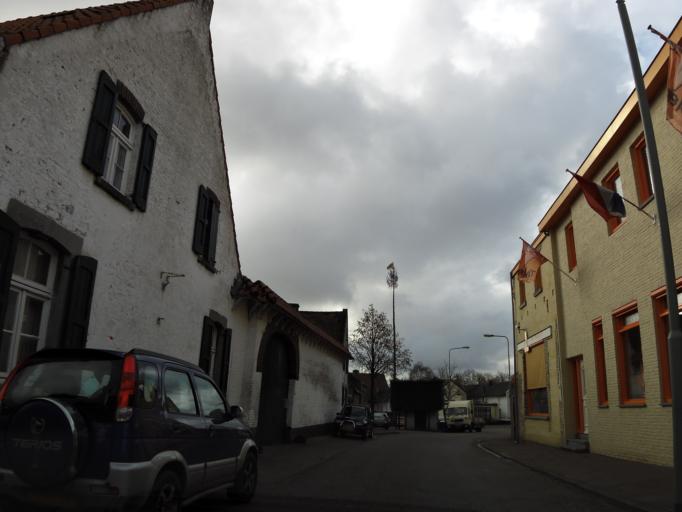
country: NL
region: Limburg
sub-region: Gemeente Maastricht
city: Heer
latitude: 50.8072
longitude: 5.7665
